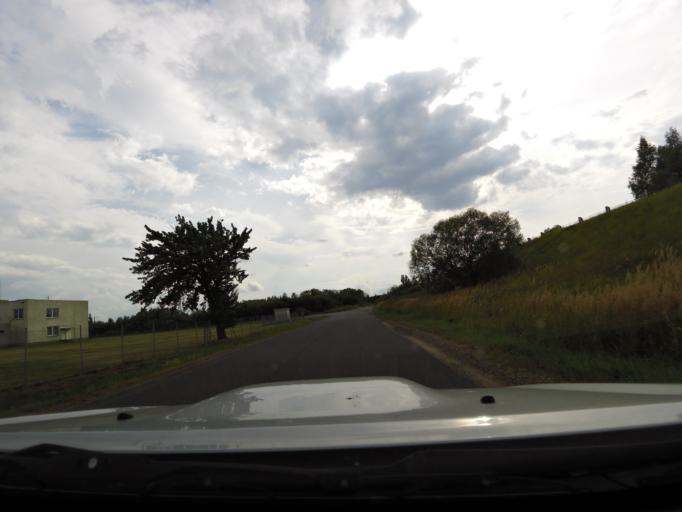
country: LT
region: Vilnius County
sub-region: Vilniaus Rajonas
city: Vievis
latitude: 54.7840
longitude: 24.8081
